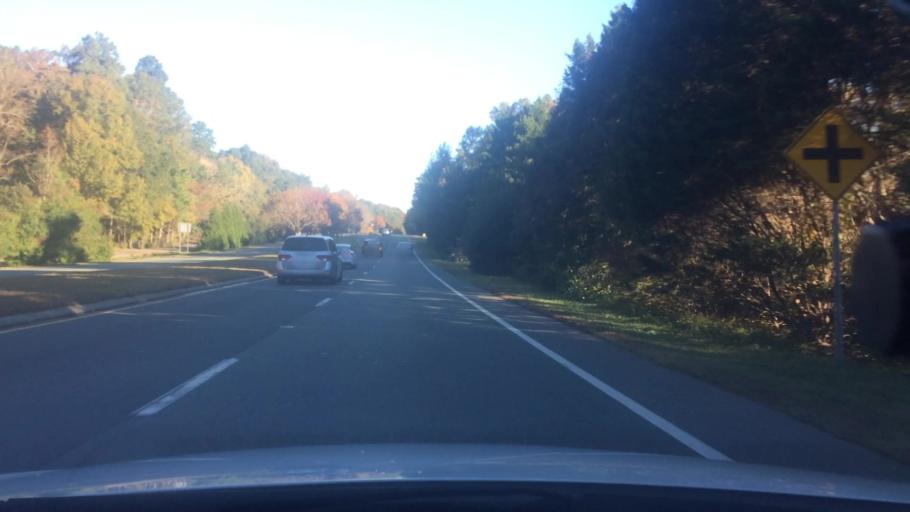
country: US
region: North Carolina
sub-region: Orange County
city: Chapel Hill
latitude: 35.9133
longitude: -79.0264
